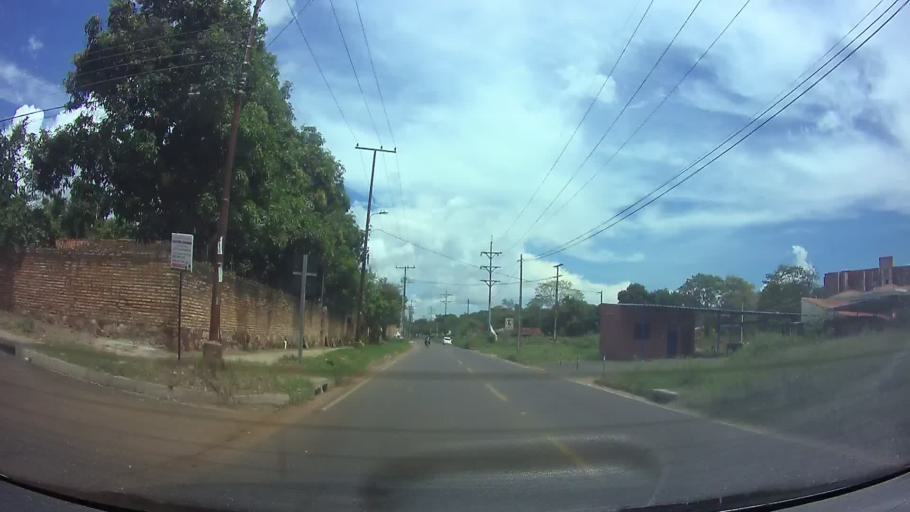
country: PY
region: Central
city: Fernando de la Mora
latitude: -25.3143
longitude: -57.5230
